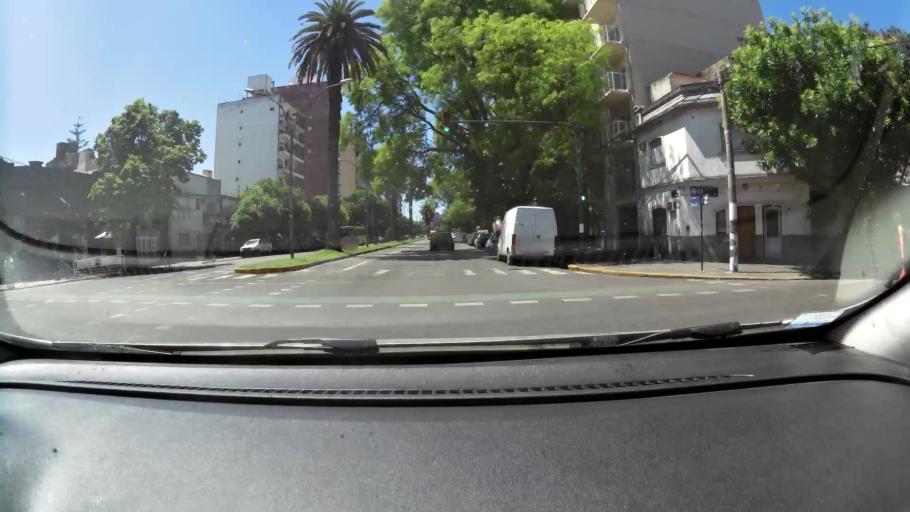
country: AR
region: Santa Fe
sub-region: Departamento de Rosario
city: Rosario
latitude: -32.9441
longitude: -60.6661
